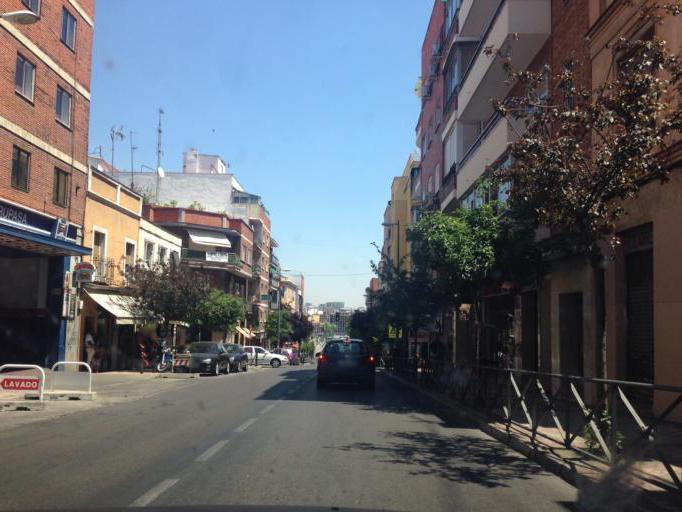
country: ES
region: Madrid
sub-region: Provincia de Madrid
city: Usera
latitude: 40.3870
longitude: -3.7013
